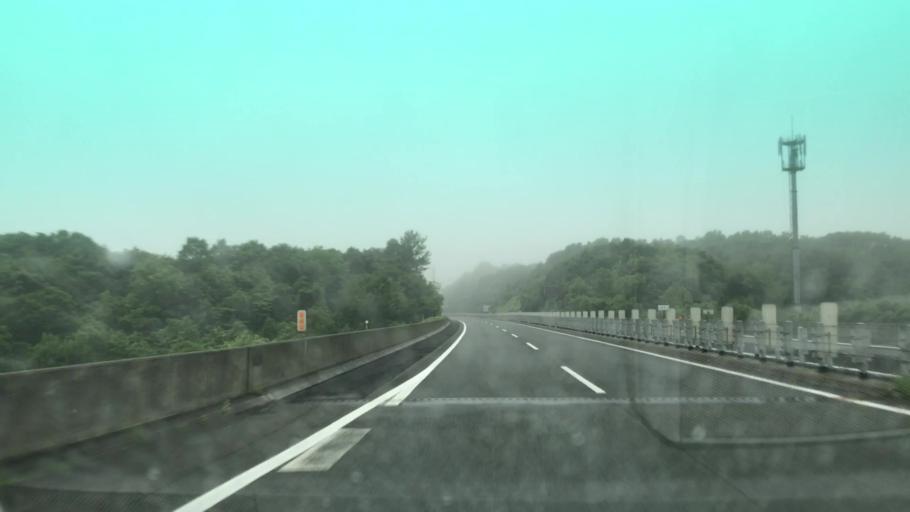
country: JP
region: Hokkaido
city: Tomakomai
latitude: 42.6303
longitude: 141.4867
